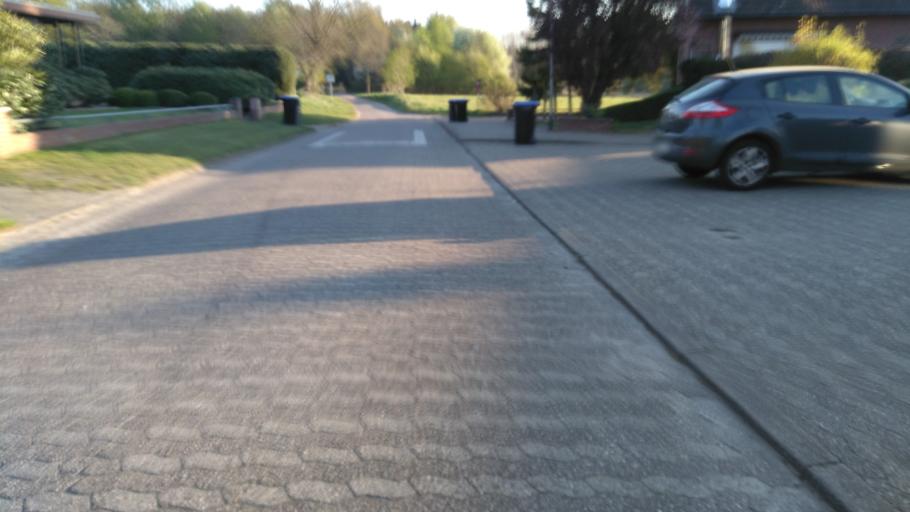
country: DE
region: Lower Saxony
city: Harsefeld
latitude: 53.4701
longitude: 9.5099
